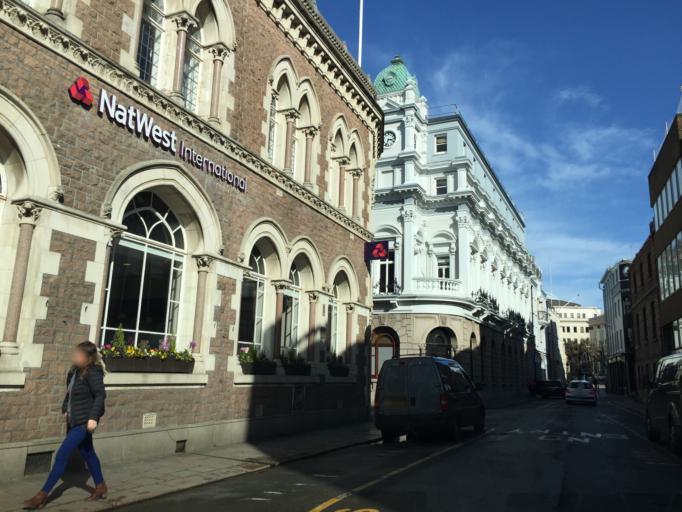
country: JE
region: St Helier
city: Saint Helier
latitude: 49.1841
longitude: -2.1072
